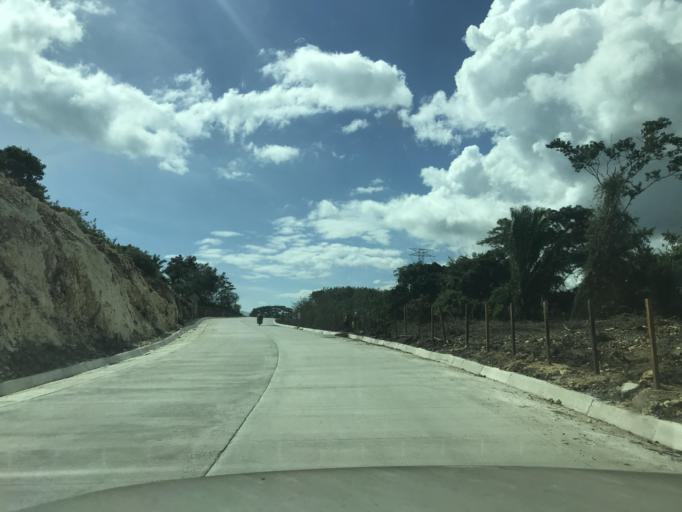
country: GT
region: Izabal
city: Morales
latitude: 15.6413
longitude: -89.0333
